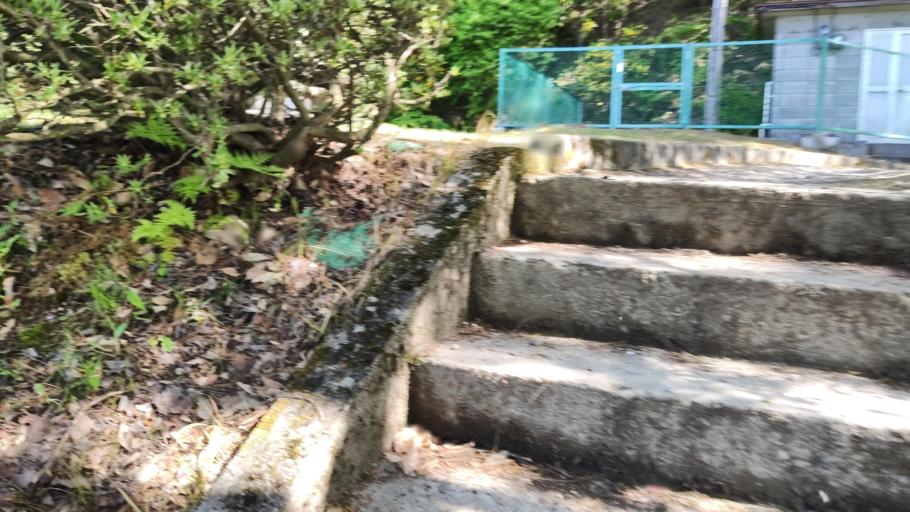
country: JP
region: Yamagata
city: Tendo
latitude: 38.3516
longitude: 140.3758
